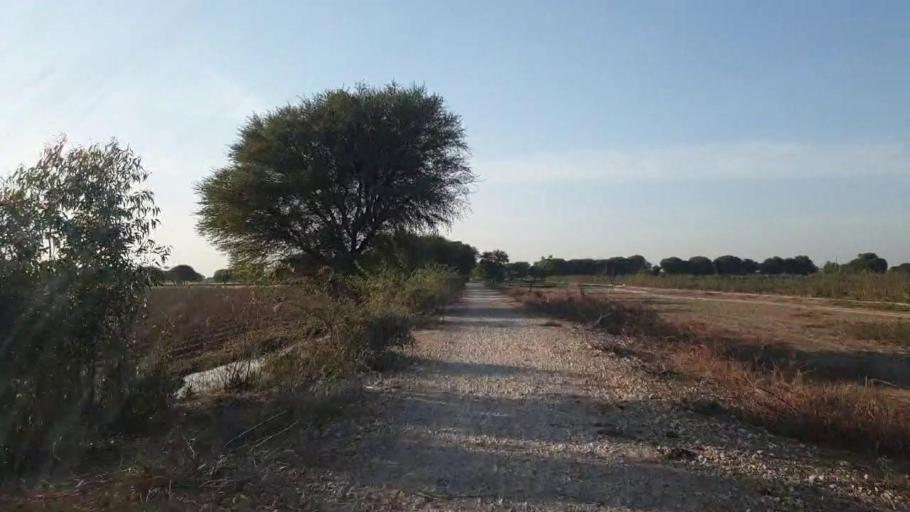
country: PK
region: Sindh
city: Chambar
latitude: 25.2800
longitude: 68.8056
